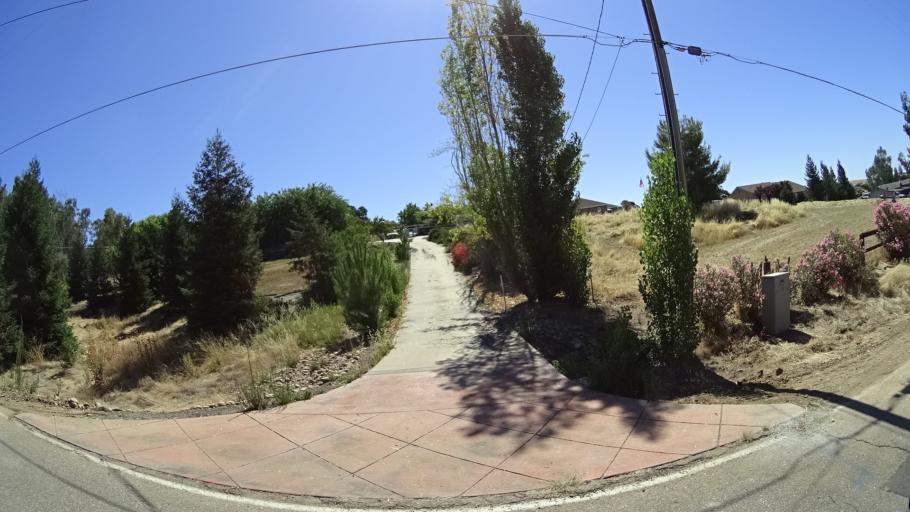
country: US
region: California
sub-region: Calaveras County
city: Rancho Calaveras
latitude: 38.1047
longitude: -120.8714
